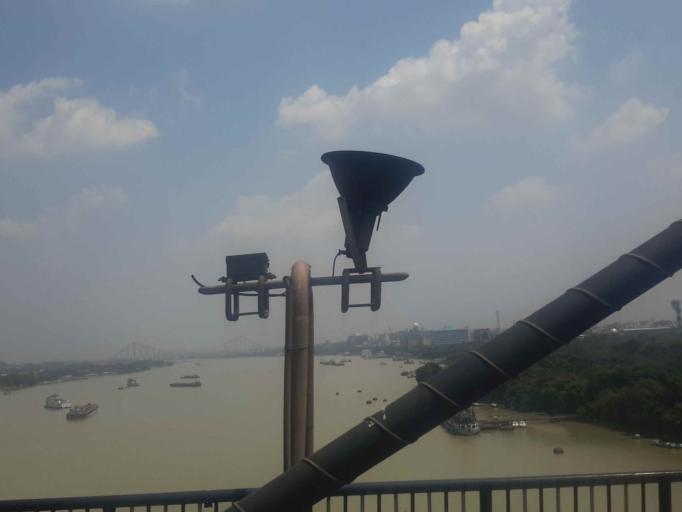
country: IN
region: West Bengal
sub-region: Haora
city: Haora
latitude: 22.5563
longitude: 88.3290
